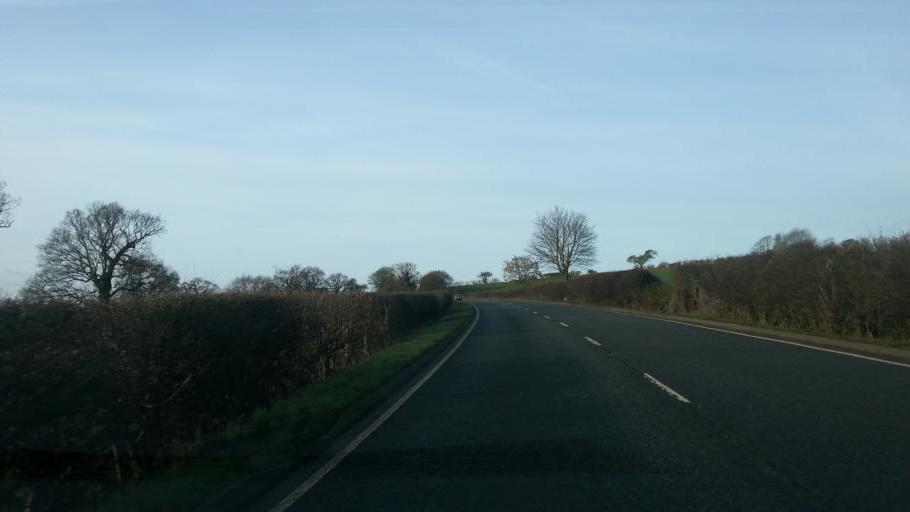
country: GB
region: England
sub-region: Leicestershire
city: Wymondham
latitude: 52.8478
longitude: -0.7784
